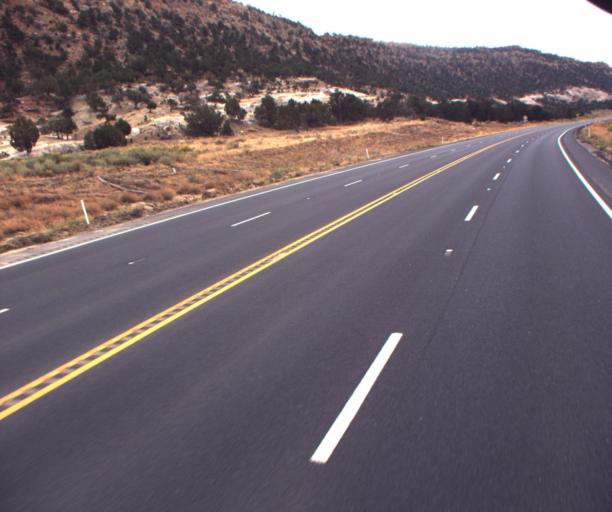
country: US
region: Arizona
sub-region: Navajo County
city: Kayenta
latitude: 36.5795
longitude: -110.4729
